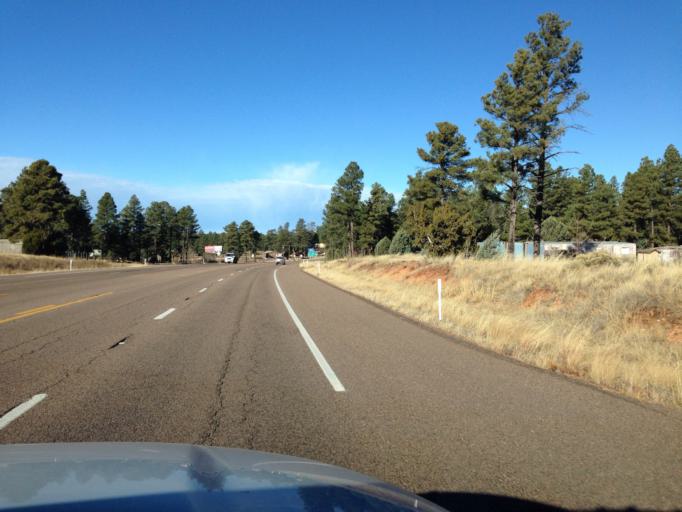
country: US
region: Arizona
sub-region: Navajo County
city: Heber-Overgaard
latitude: 34.3894
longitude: -110.5486
